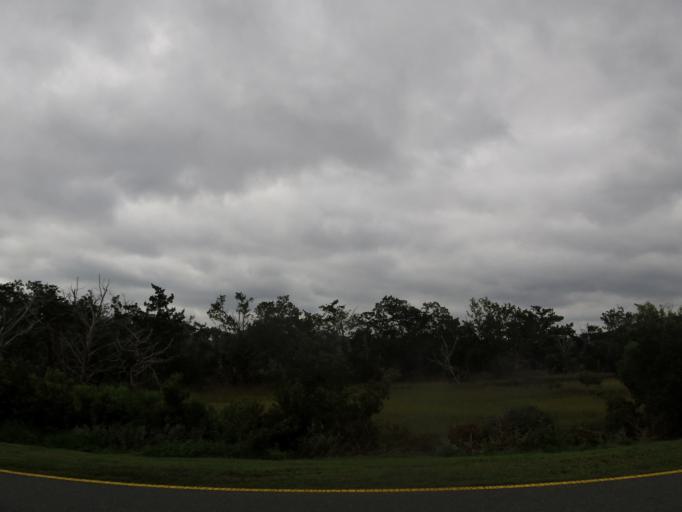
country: US
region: Georgia
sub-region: Glynn County
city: Saint Simon Mills
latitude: 31.1631
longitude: -81.4087
